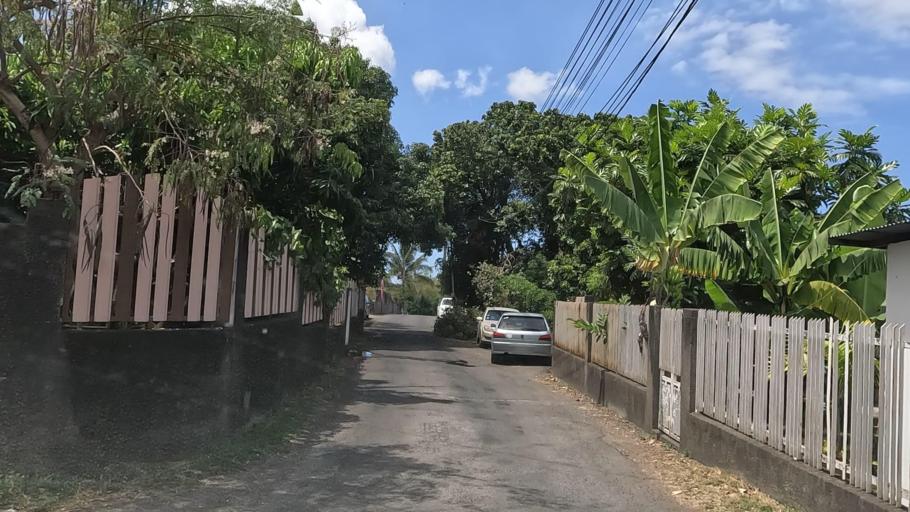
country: RE
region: Reunion
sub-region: Reunion
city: Saint-Louis
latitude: -21.2777
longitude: 55.4452
